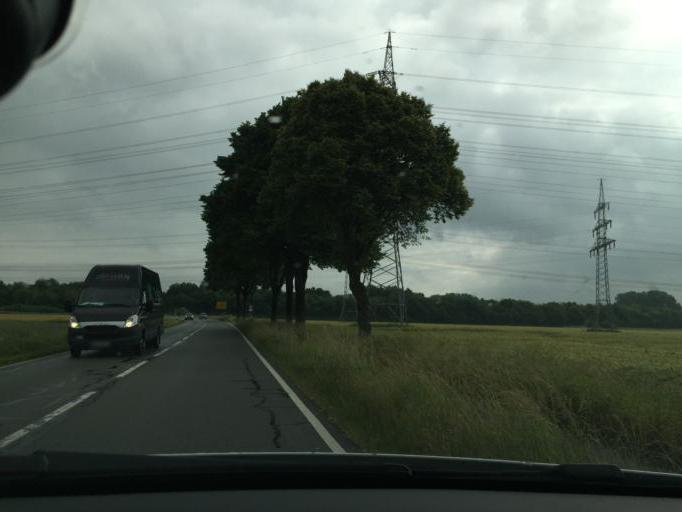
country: DE
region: Lower Saxony
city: Hameln
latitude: 52.0429
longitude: 9.3667
